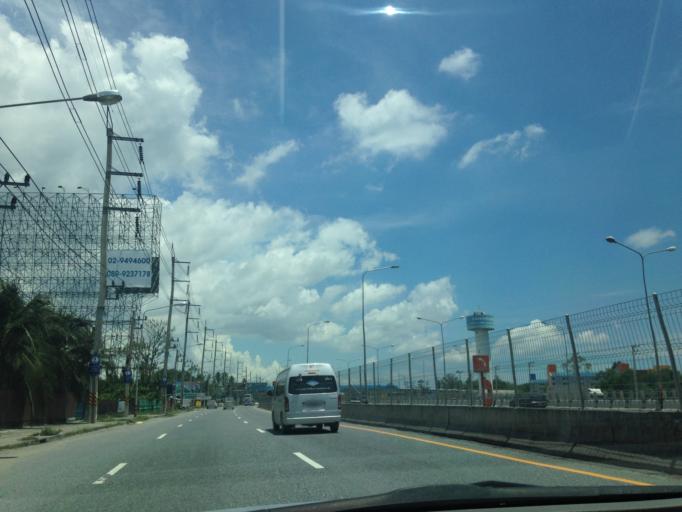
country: TH
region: Chon Buri
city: Si Racha
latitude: 13.2121
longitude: 101.0057
